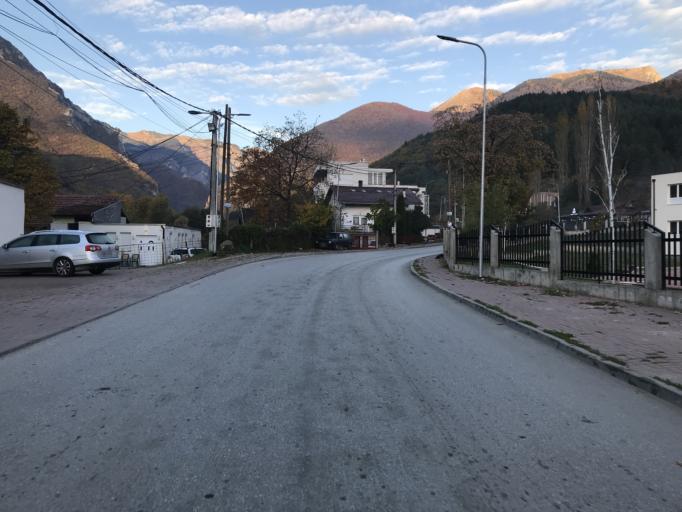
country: XK
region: Pec
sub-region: Komuna e Pejes
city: Peje
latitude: 42.6606
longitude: 20.2727
